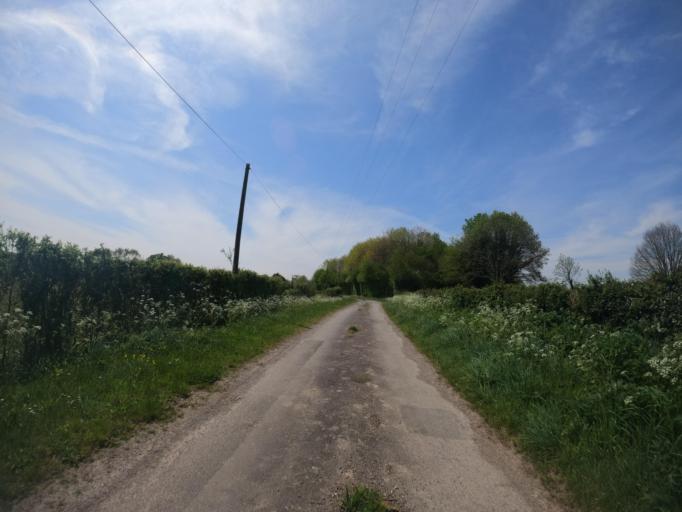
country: FR
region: Poitou-Charentes
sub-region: Departement des Deux-Sevres
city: Moncoutant
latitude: 46.6554
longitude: -0.5218
